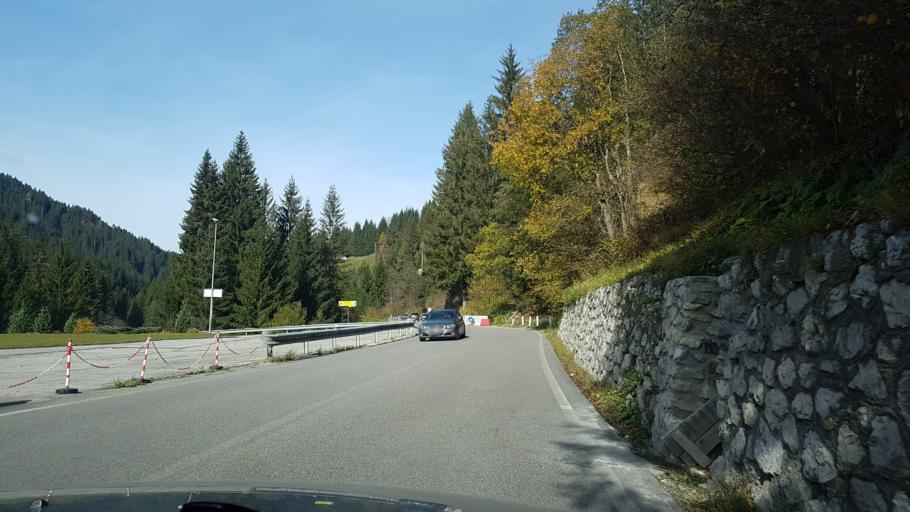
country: IT
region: Veneto
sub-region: Provincia di Belluno
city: Santo Stefano di Cadore
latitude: 46.5644
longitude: 12.5445
